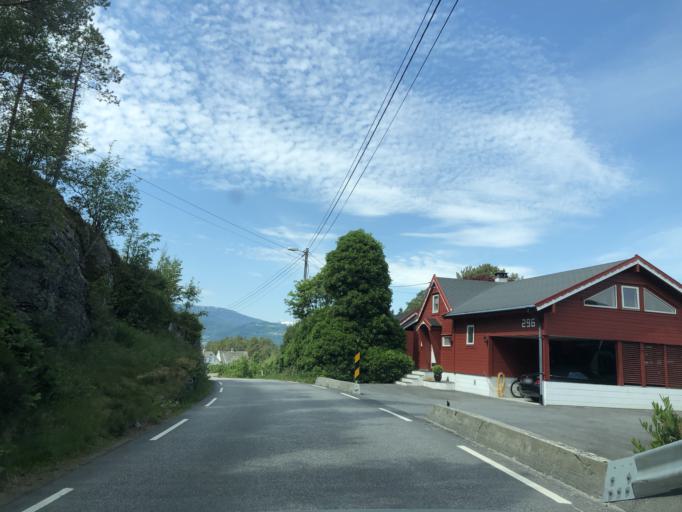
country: NO
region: Hordaland
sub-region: Jondal
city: Jondal
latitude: 60.3054
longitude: 6.2791
